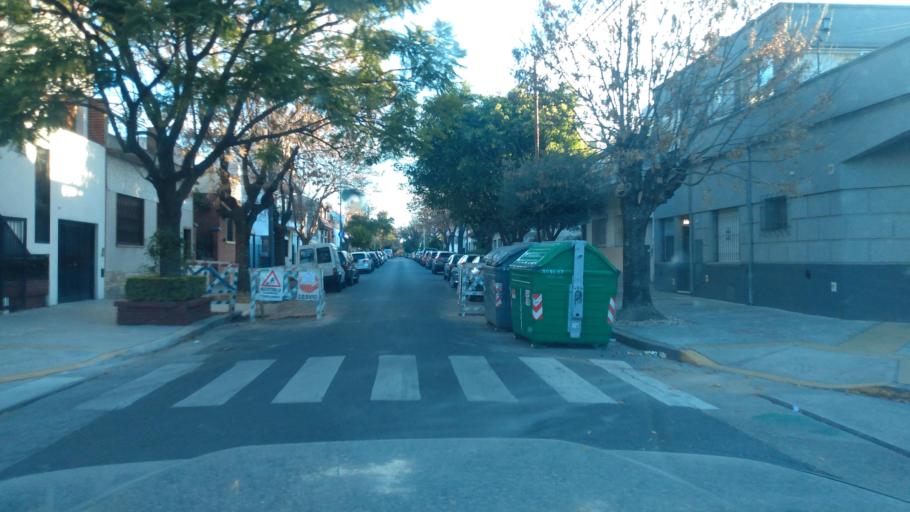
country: AR
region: Buenos Aires F.D.
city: Villa Santa Rita
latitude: -34.5846
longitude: -58.4865
